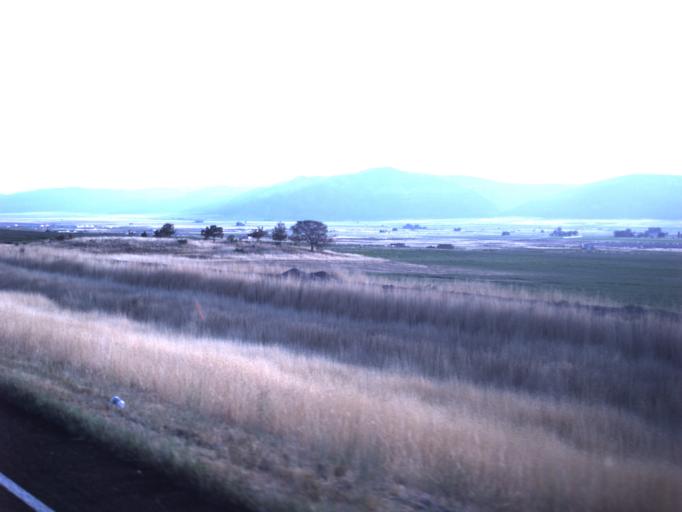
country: US
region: Utah
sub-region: Sanpete County
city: Moroni
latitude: 39.4750
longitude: -111.5270
